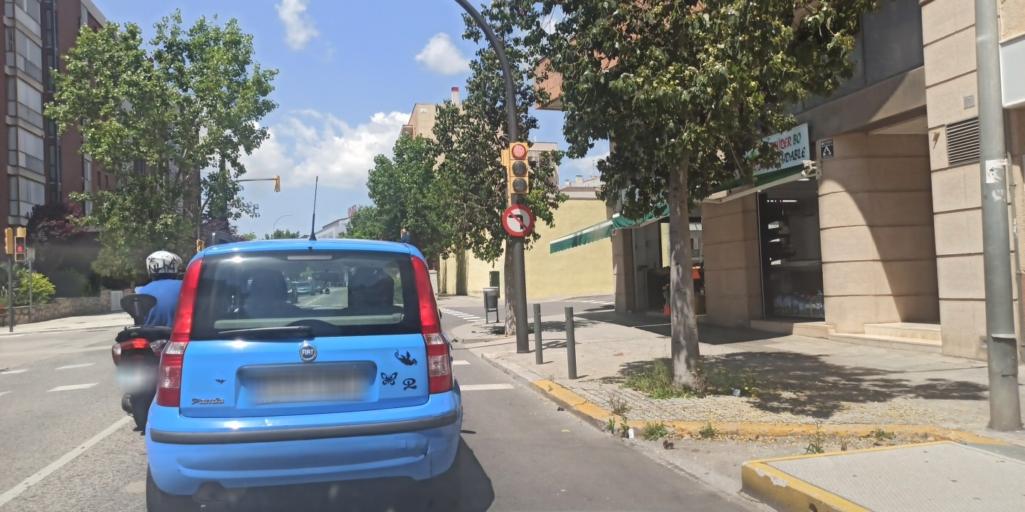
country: ES
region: Catalonia
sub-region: Provincia de Barcelona
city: Vilafranca del Penedes
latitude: 41.3399
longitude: 1.6949
